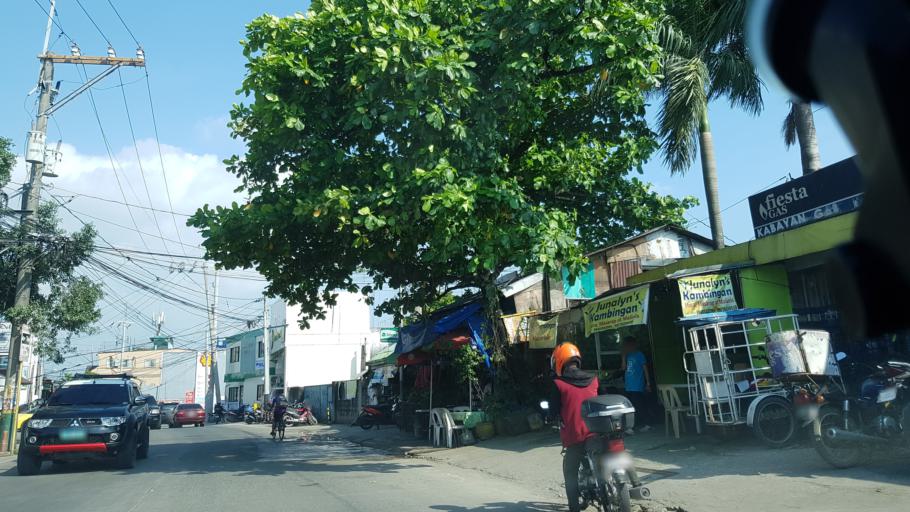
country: PH
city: Sambayanihan People's Village
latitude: 14.4877
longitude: 121.0242
